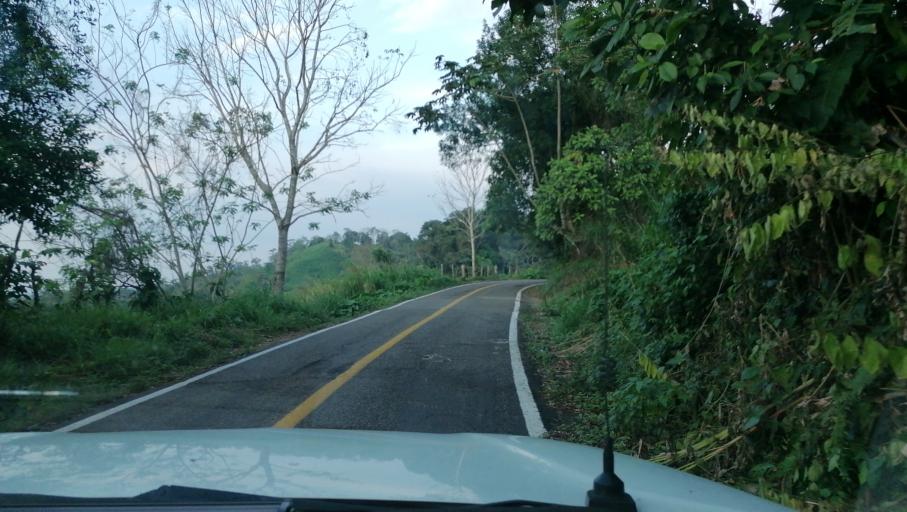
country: MX
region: Chiapas
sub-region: Juarez
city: El Triunfo 1ra. Seccion (Cardona)
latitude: 17.5019
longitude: -93.2379
